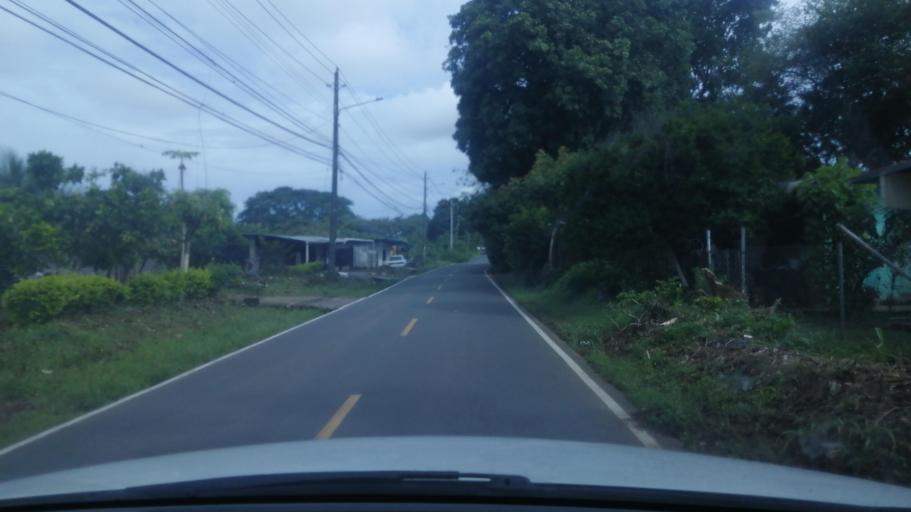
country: PA
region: Chiriqui
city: David
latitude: 8.4126
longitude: -82.4266
